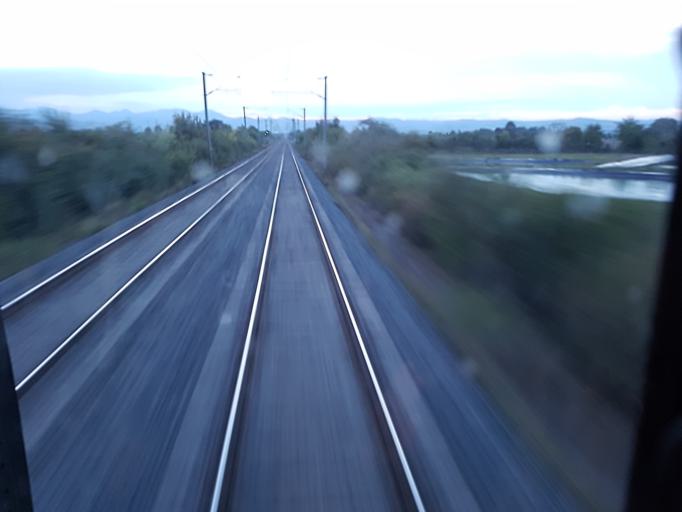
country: FR
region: Auvergne
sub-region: Departement du Puy-de-Dome
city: Ennezat
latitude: 45.9074
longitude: 3.1906
